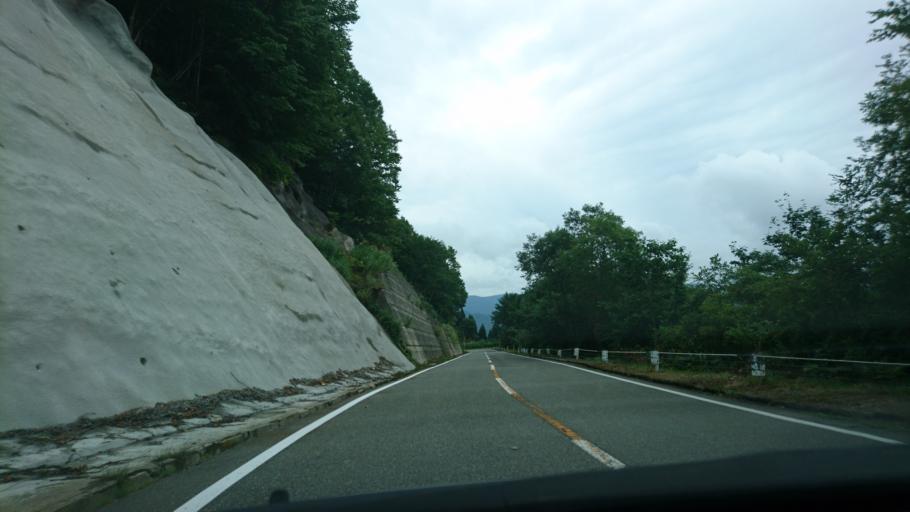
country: JP
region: Akita
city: Yuzawa
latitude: 38.9799
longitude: 140.7211
